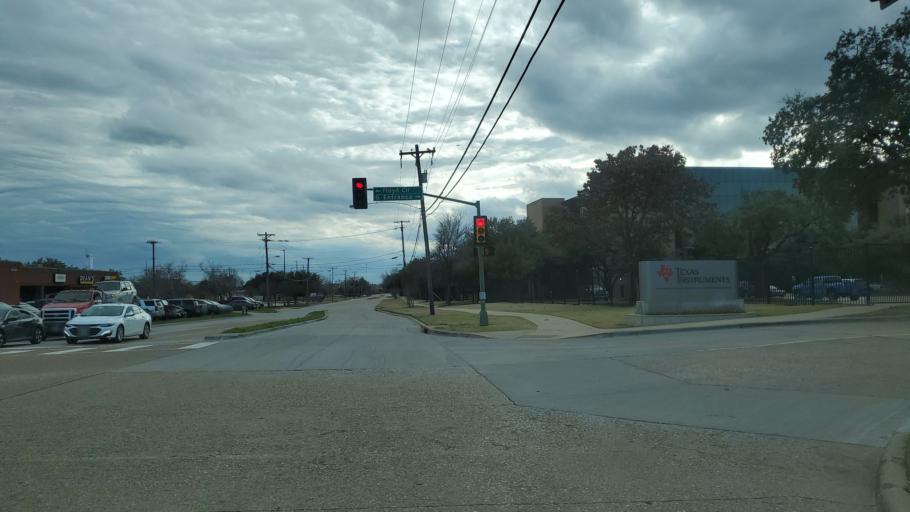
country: US
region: Texas
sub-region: Dallas County
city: Richardson
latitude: 32.9314
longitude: -96.7489
